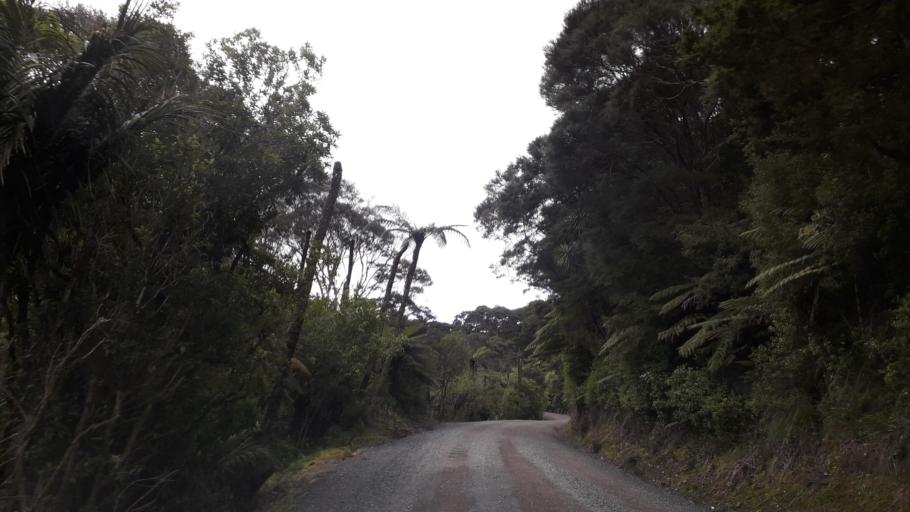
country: NZ
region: Northland
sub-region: Far North District
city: Paihia
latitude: -35.3198
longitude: 174.2332
